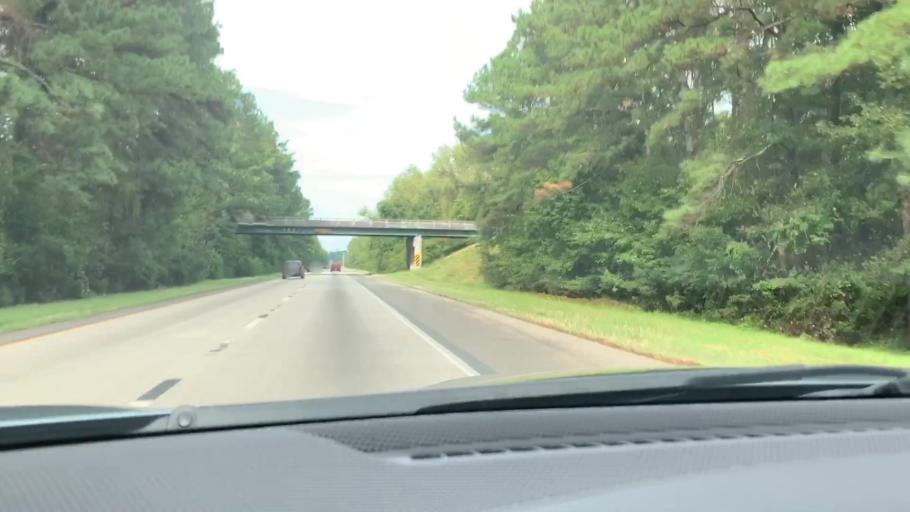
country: US
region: South Carolina
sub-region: Colleton County
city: Walterboro
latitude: 32.8948
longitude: -80.7096
